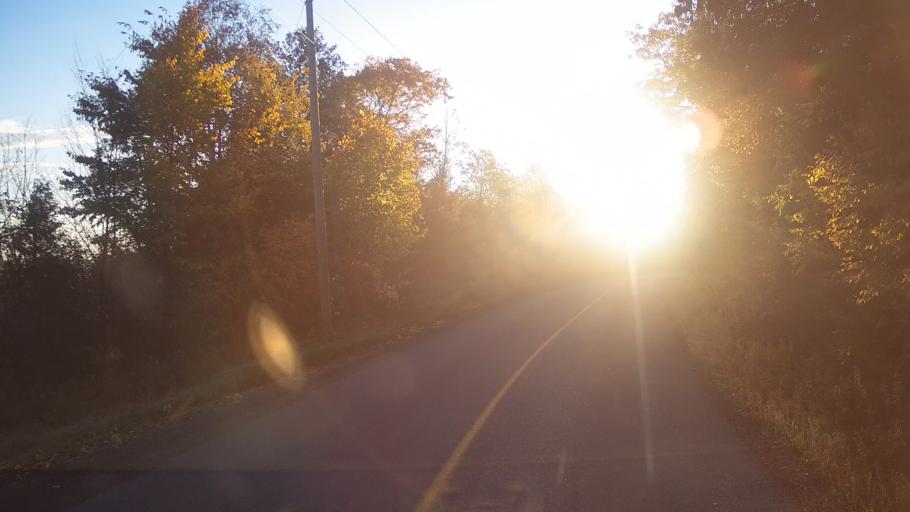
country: CA
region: Ontario
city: Arnprior
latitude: 45.3473
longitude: -76.3394
